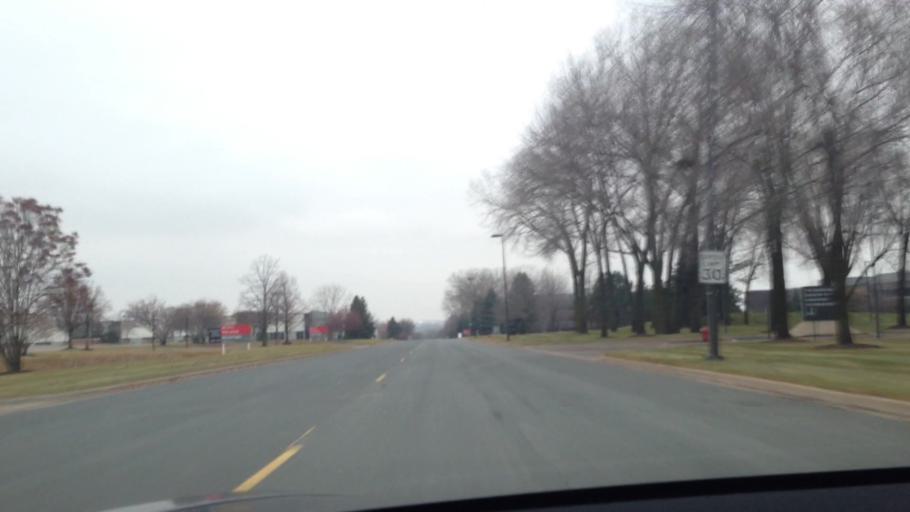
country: US
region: Minnesota
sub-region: Dakota County
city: Mendota Heights
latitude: 44.8636
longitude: -93.1569
